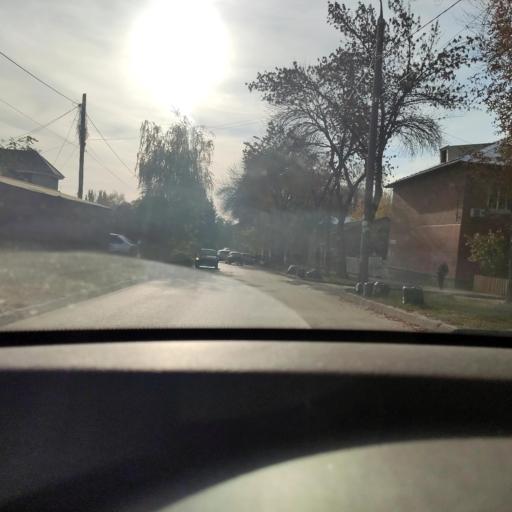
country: RU
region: Samara
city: Samara
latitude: 53.2283
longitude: 50.2408
